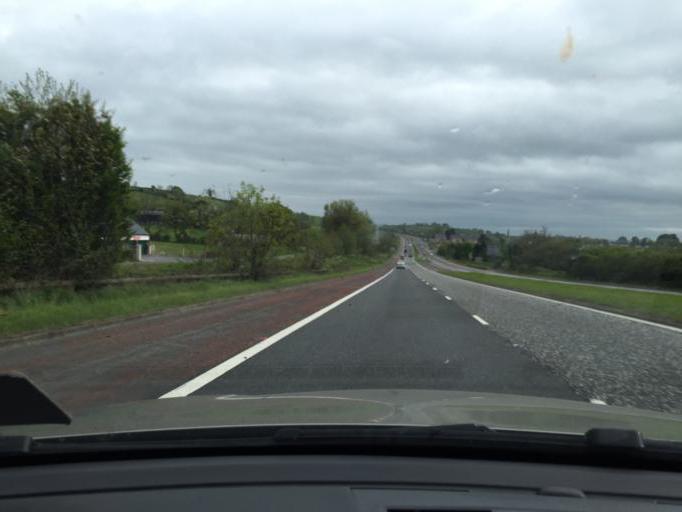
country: GB
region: Northern Ireland
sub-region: Banbridge District
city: Banbridge
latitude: 54.3253
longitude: -6.2959
